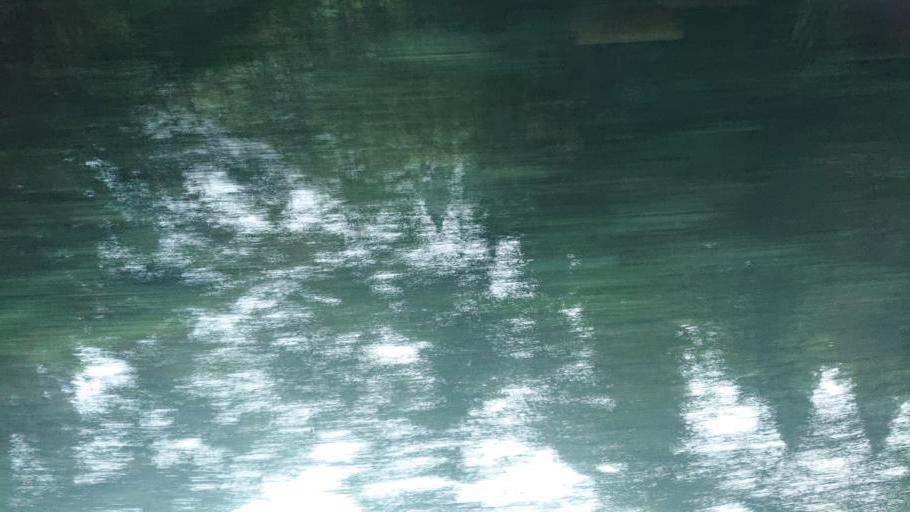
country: TW
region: Taiwan
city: Lugu
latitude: 23.5108
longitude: 120.7014
